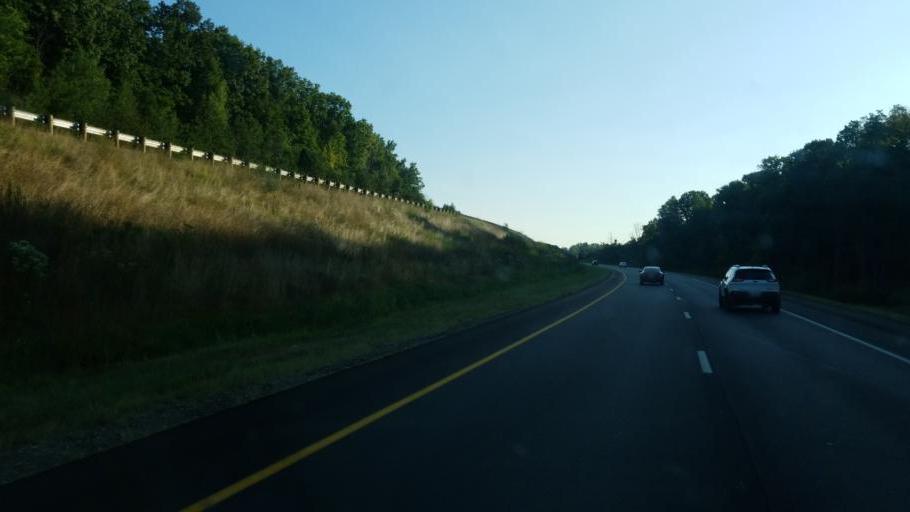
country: US
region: Ohio
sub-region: Summit County
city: Richfield
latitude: 41.2361
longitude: -81.5972
